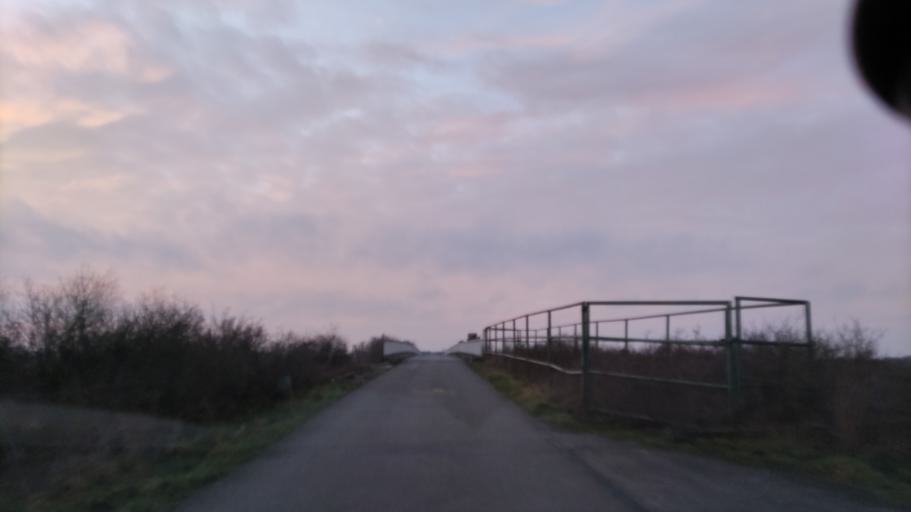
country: DE
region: Lower Saxony
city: Echem
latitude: 53.3385
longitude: 10.4996
